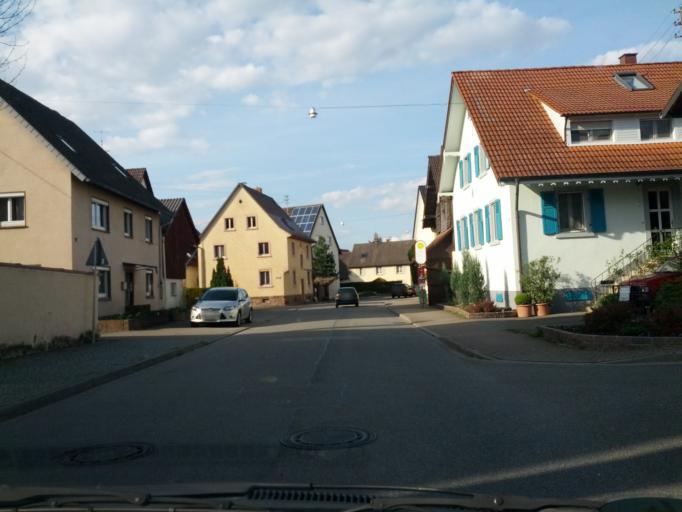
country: DE
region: Baden-Wuerttemberg
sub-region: Freiburg Region
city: Umkirch
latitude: 48.0701
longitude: 7.7709
